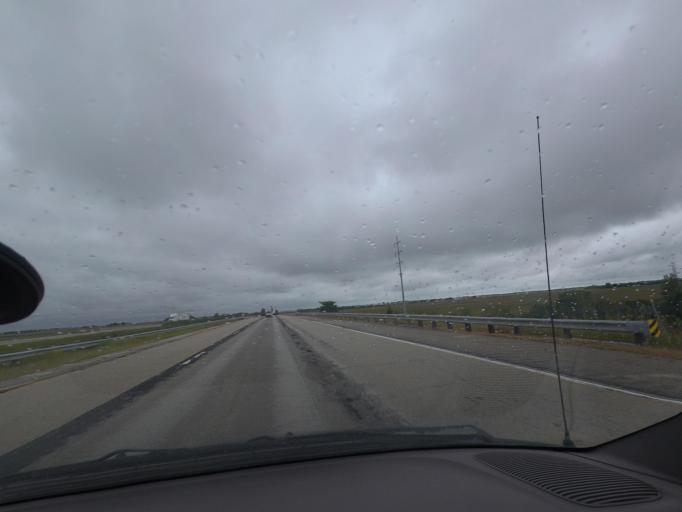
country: US
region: Illinois
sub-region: Macon County
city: Harristown
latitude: 39.8521
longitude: -89.0456
